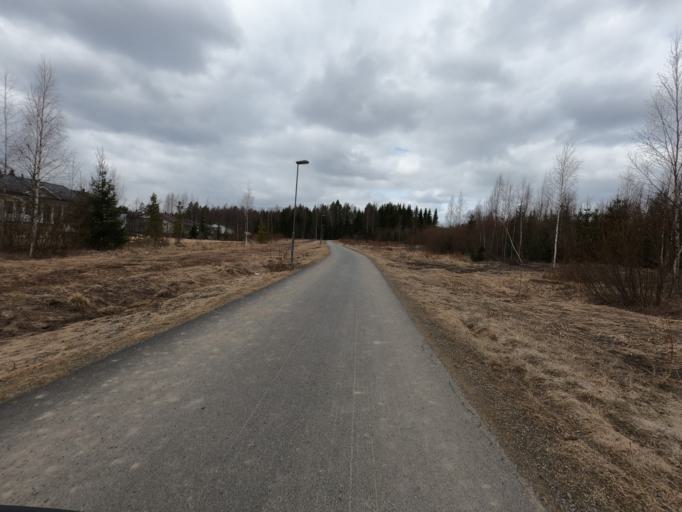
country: FI
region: North Karelia
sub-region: Joensuu
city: Joensuu
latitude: 62.5681
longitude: 29.8162
